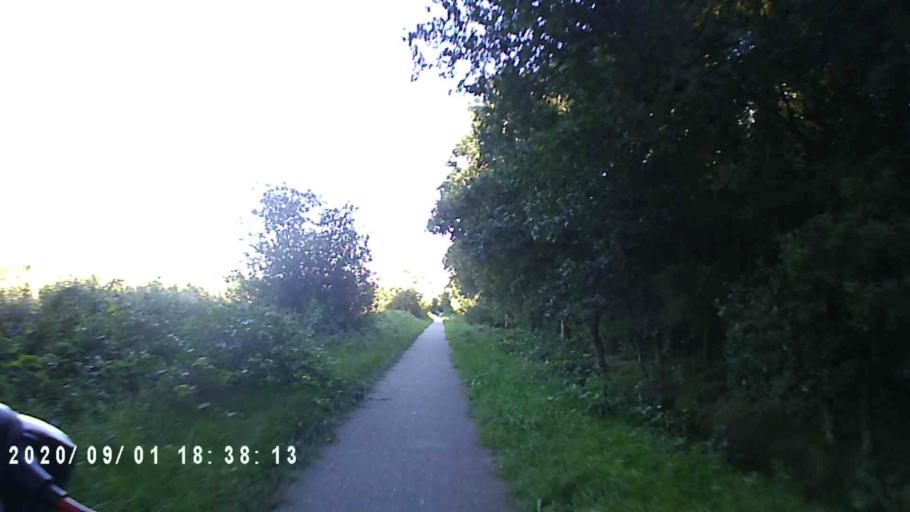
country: NL
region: Groningen
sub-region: Gemeente Hoogezand-Sappemeer
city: Sappemeer
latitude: 53.1466
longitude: 6.8144
